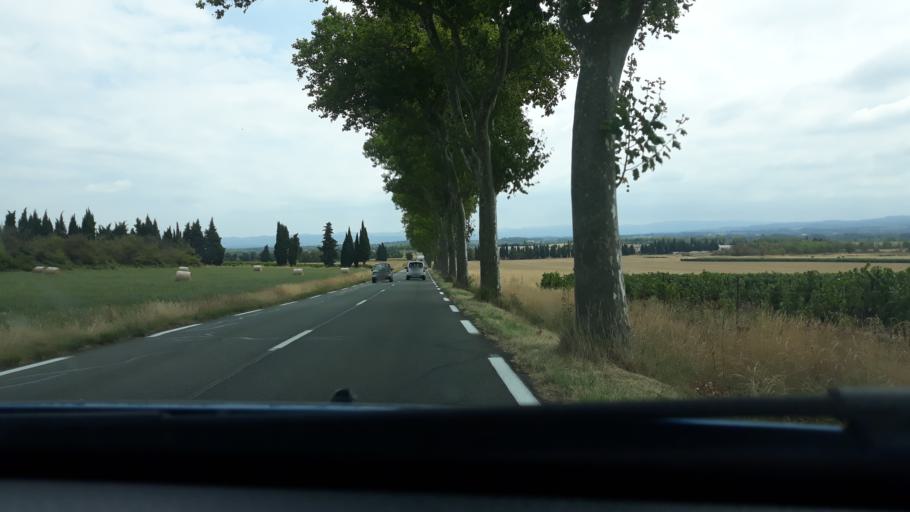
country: FR
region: Languedoc-Roussillon
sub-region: Departement de l'Aude
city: Pezens
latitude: 43.2710
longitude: 2.2368
